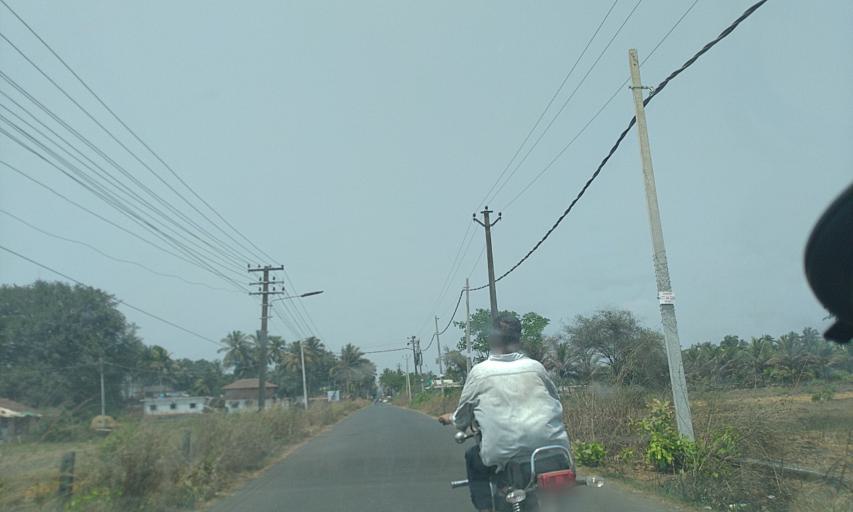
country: IN
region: Goa
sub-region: North Goa
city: Saligao
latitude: 15.5500
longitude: 73.8063
